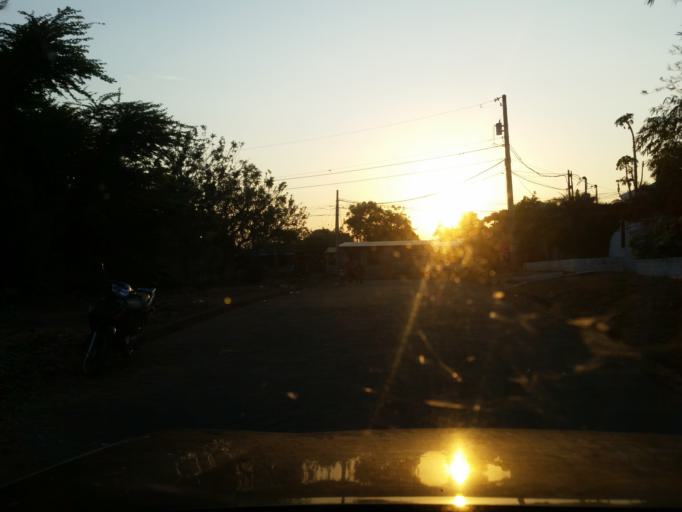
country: NI
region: Granada
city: Granada
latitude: 11.9486
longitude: -85.9460
